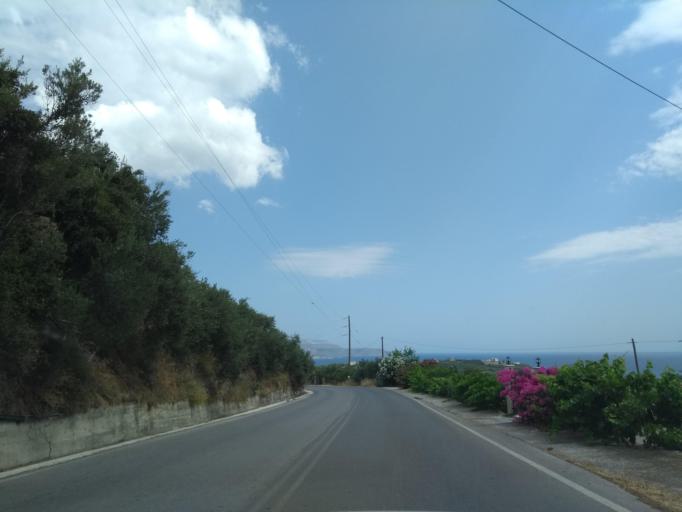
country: GR
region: Crete
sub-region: Nomos Chanias
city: Kalivai
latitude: 35.4371
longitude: 24.1756
